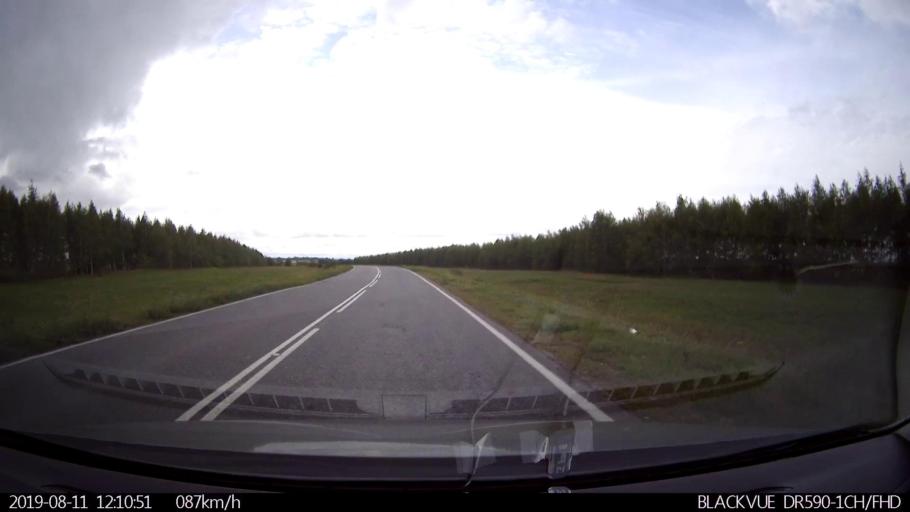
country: RU
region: Ulyanovsk
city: Silikatnyy
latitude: 53.9900
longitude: 48.0146
